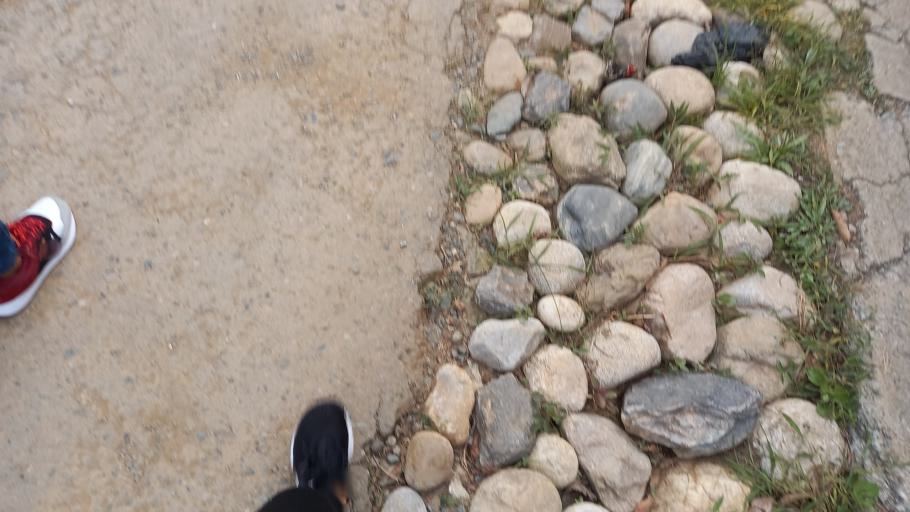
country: CO
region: Antioquia
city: Santa Barbara
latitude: 5.8383
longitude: -75.5741
